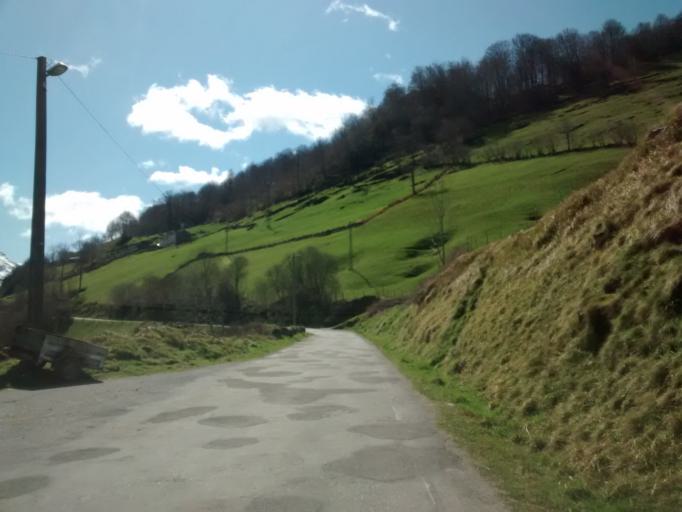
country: ES
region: Cantabria
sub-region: Provincia de Cantabria
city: Vega de Pas
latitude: 43.2085
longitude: -3.7029
